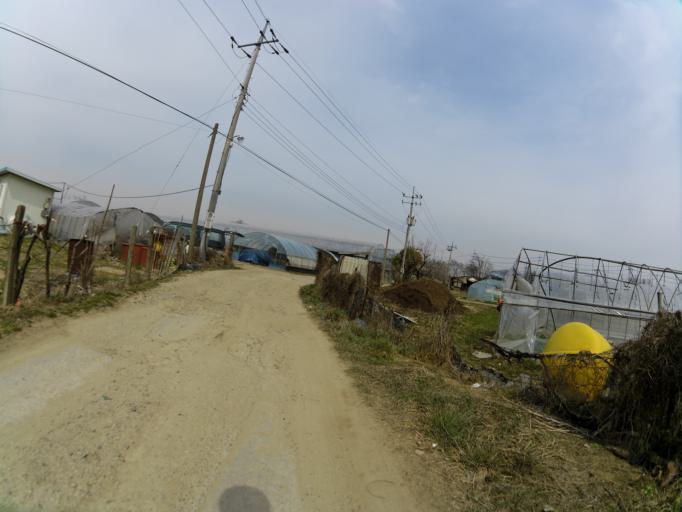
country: KR
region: Gyeongsangbuk-do
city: Gyeongsan-si
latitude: 35.8587
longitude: 128.7162
